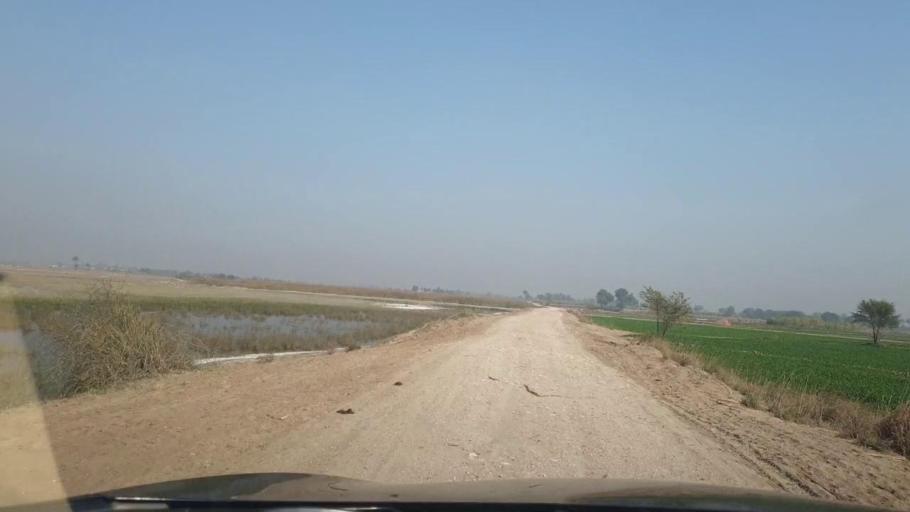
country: PK
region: Sindh
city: Ubauro
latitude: 28.1285
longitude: 69.7508
